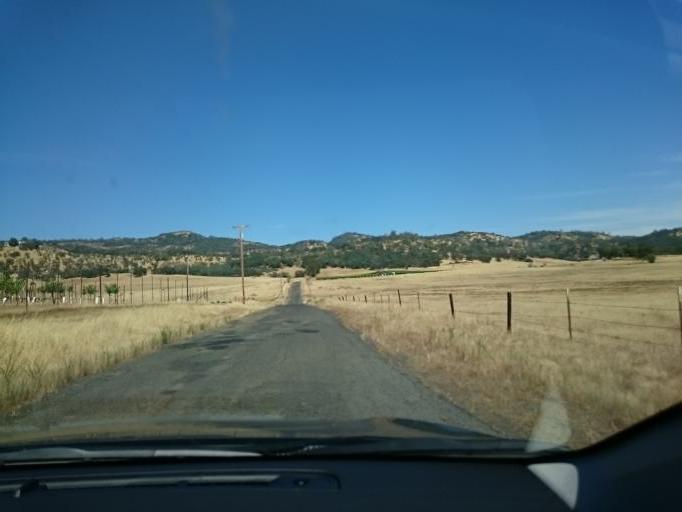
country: US
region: California
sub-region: Calaveras County
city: Copperopolis
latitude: 38.0488
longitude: -120.7013
